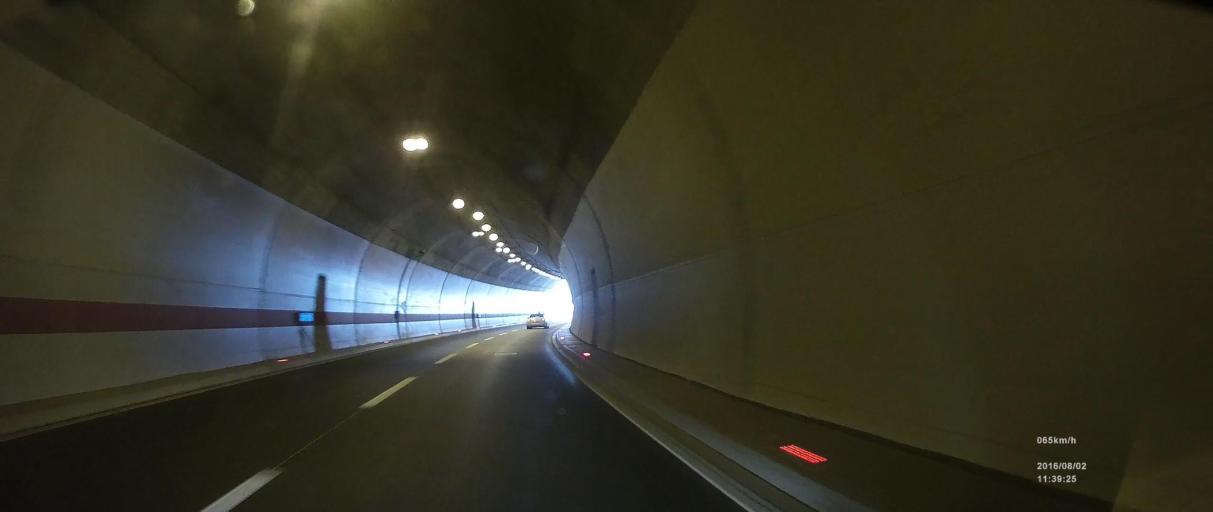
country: HR
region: Dubrovacko-Neretvanska
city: Komin
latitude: 43.0863
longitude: 17.4911
